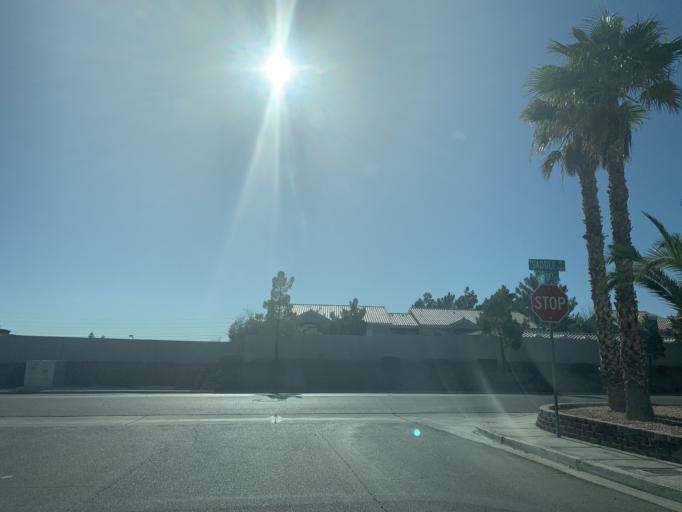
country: US
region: Nevada
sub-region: Clark County
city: Summerlin South
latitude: 36.1170
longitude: -115.2894
